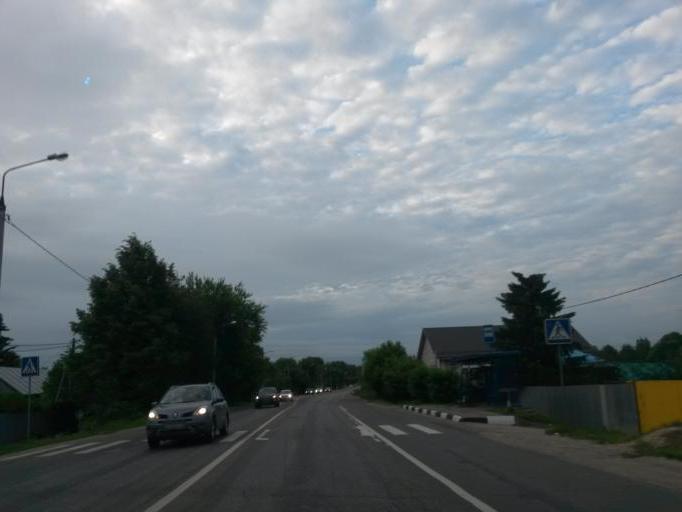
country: RU
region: Moskovskaya
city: Stolbovaya
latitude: 55.2257
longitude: 37.5034
